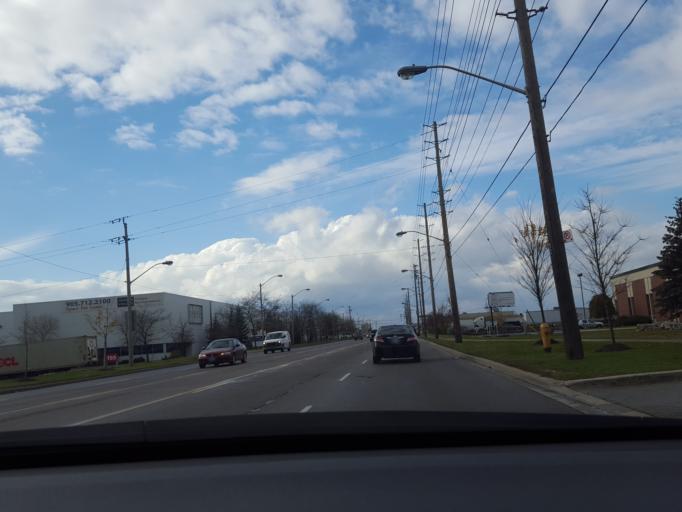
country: CA
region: Ontario
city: Etobicoke
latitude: 43.7119
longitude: -79.5724
